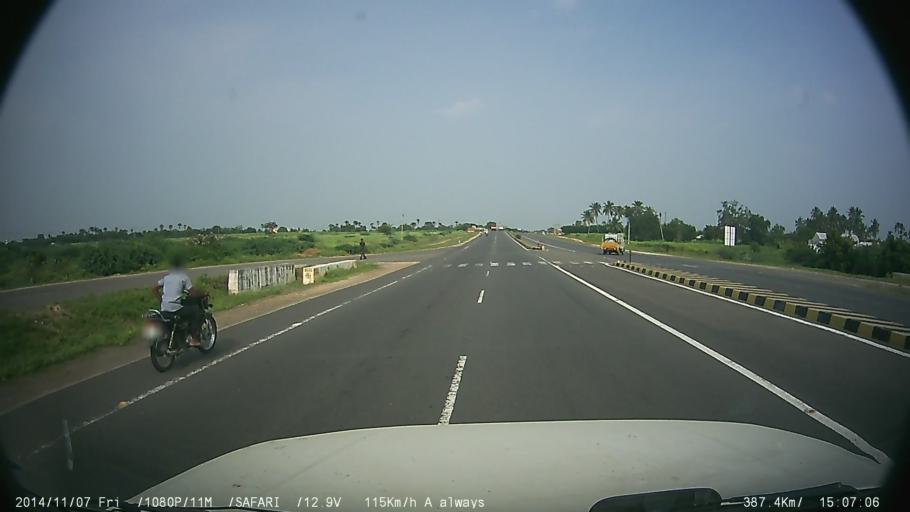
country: IN
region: Tamil Nadu
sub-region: Erode
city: Vijayapuri
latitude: 11.2344
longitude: 77.4817
